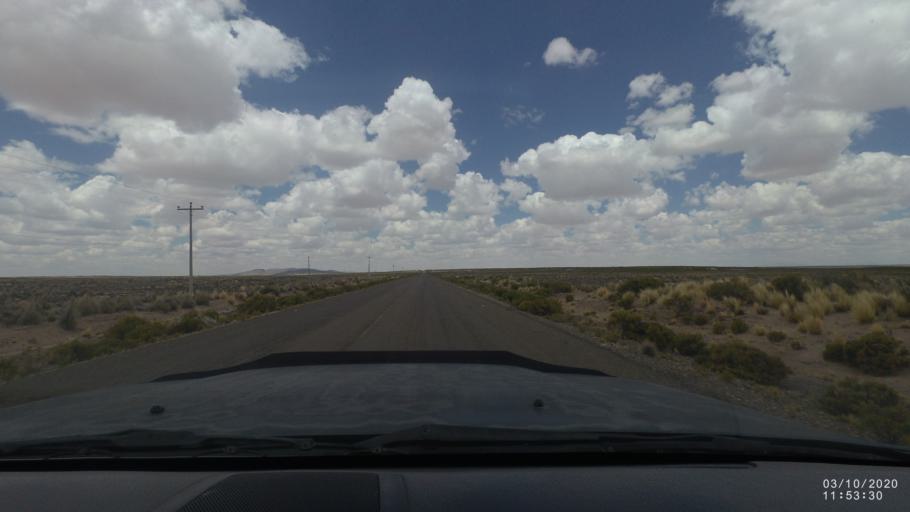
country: BO
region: Oruro
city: Poopo
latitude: -18.4800
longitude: -67.6046
